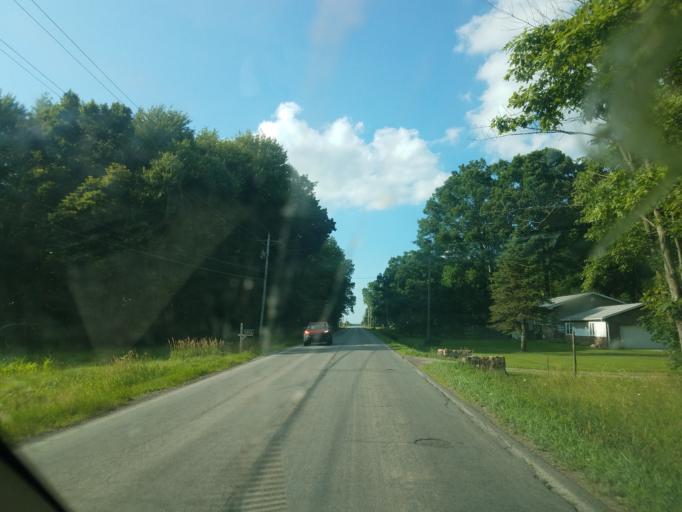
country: US
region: Ohio
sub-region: Wayne County
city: Apple Creek
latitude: 40.7397
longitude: -81.8960
